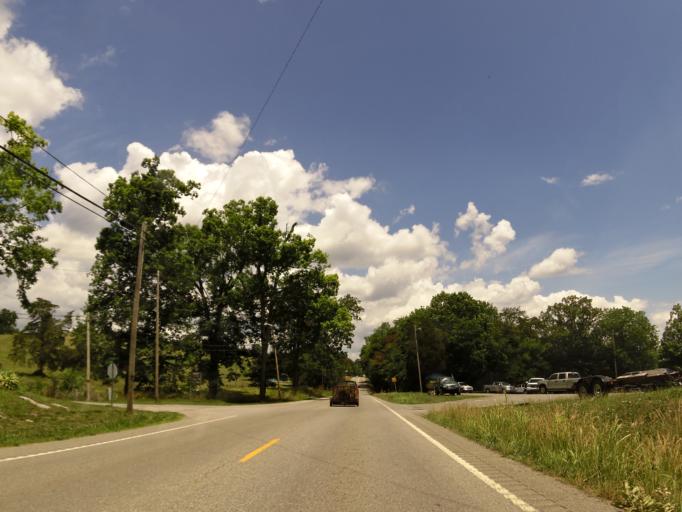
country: US
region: Tennessee
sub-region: Union County
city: Maynardville
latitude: 36.3560
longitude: -83.7320
